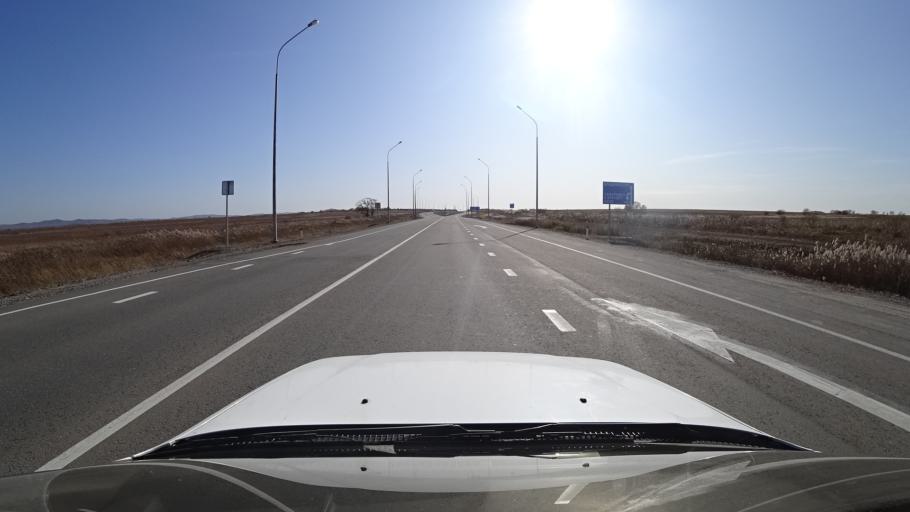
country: RU
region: Primorskiy
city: Dal'nerechensk
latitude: 45.8665
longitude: 133.7214
